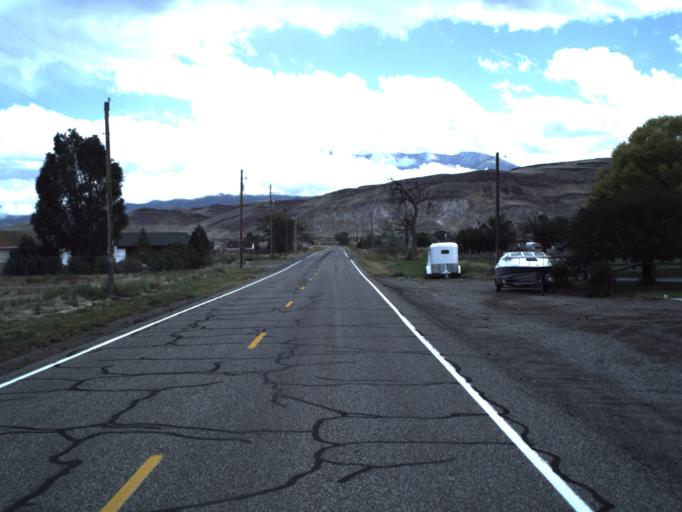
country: US
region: Utah
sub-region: Sevier County
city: Monroe
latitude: 38.6242
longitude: -112.2155
